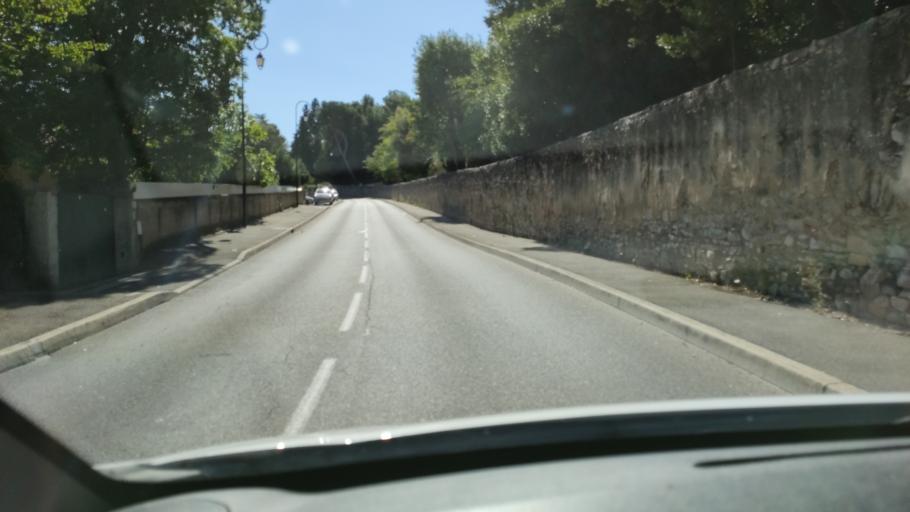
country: FR
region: Languedoc-Roussillon
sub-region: Departement du Gard
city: Villeneuve-les-Avignon
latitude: 43.9668
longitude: 4.7835
